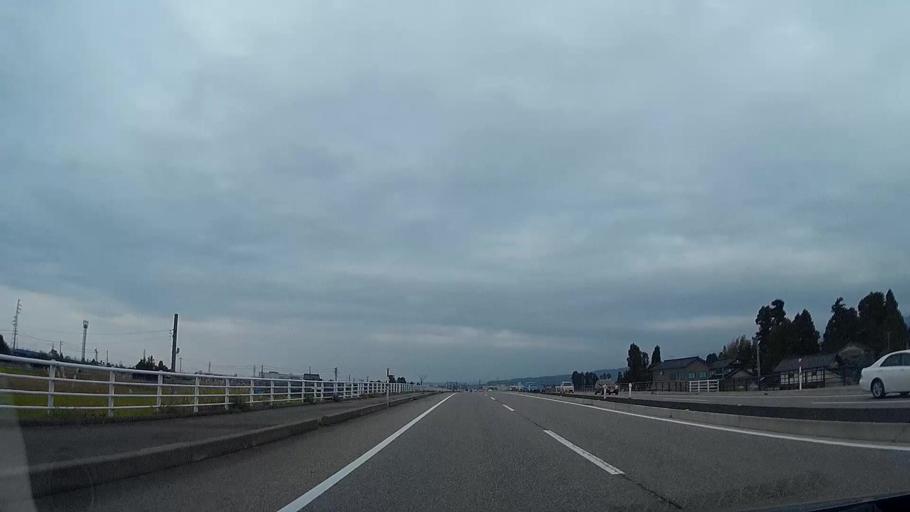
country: JP
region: Toyama
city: Uozu
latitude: 36.7698
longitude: 137.3817
